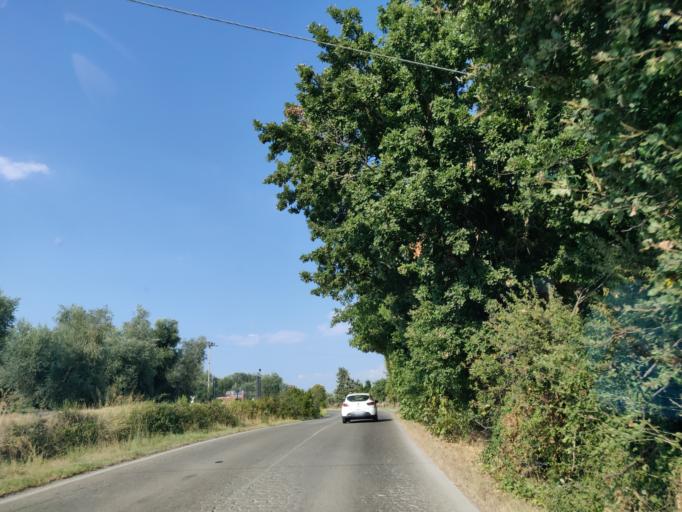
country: IT
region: Latium
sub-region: Provincia di Viterbo
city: Canino
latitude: 42.4156
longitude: 11.7027
